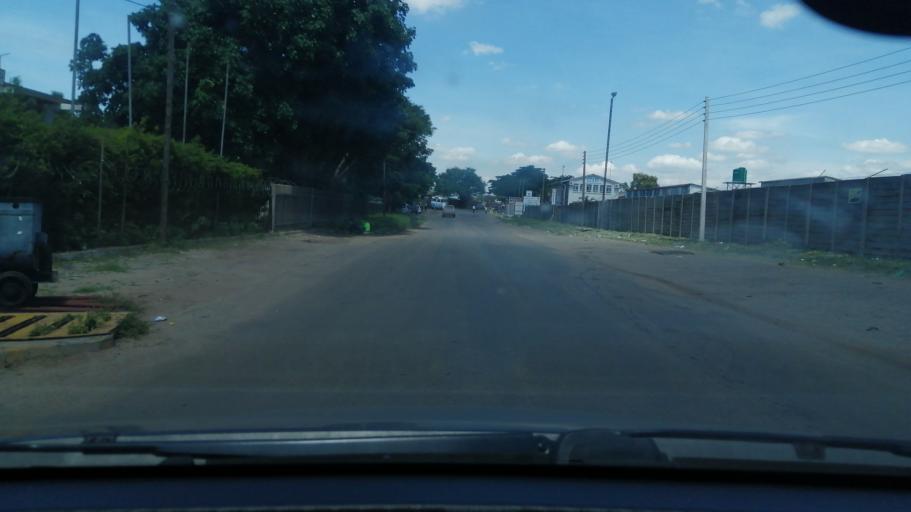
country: ZW
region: Harare
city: Epworth
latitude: -17.8443
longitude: 31.1156
